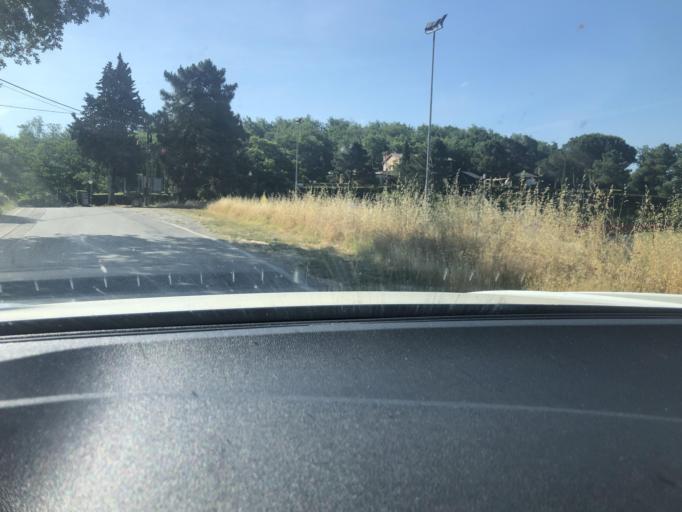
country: IT
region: Tuscany
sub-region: Provincia di Pistoia
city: Larciano
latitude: 43.8424
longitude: 10.9097
